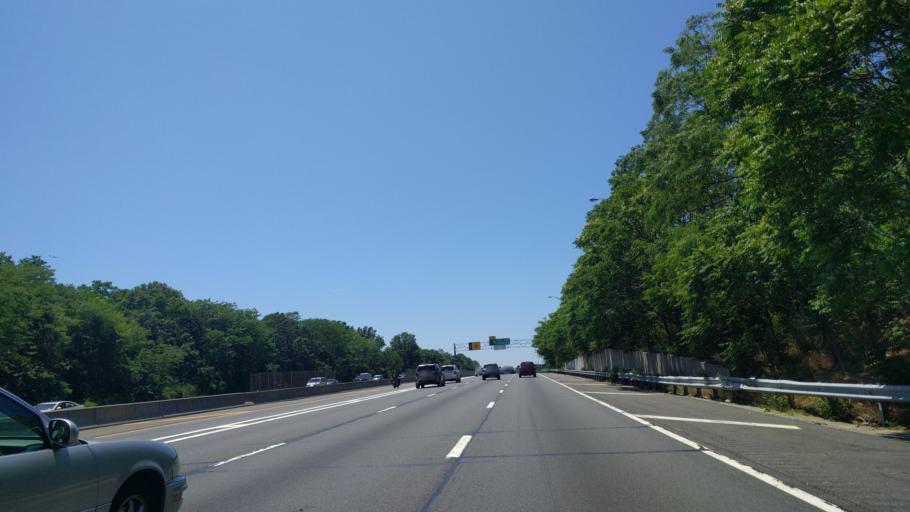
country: US
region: New York
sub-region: Suffolk County
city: Dix Hills
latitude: 40.7936
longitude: -73.3543
